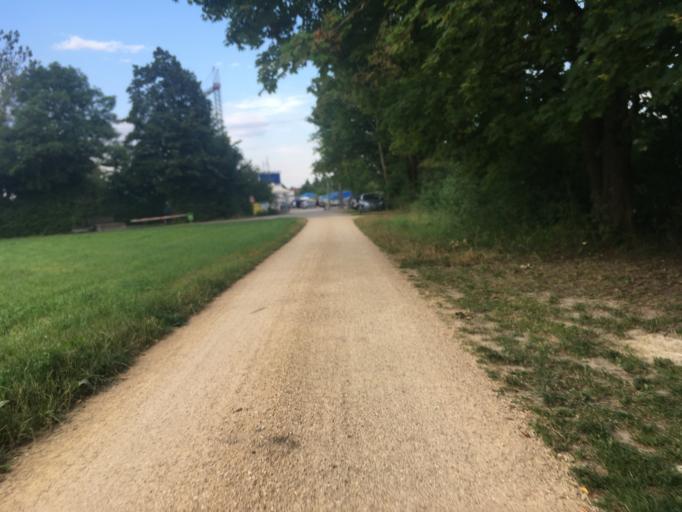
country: CH
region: Solothurn
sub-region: Bezirk Lebern
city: Langendorf
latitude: 47.1969
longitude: 7.5072
